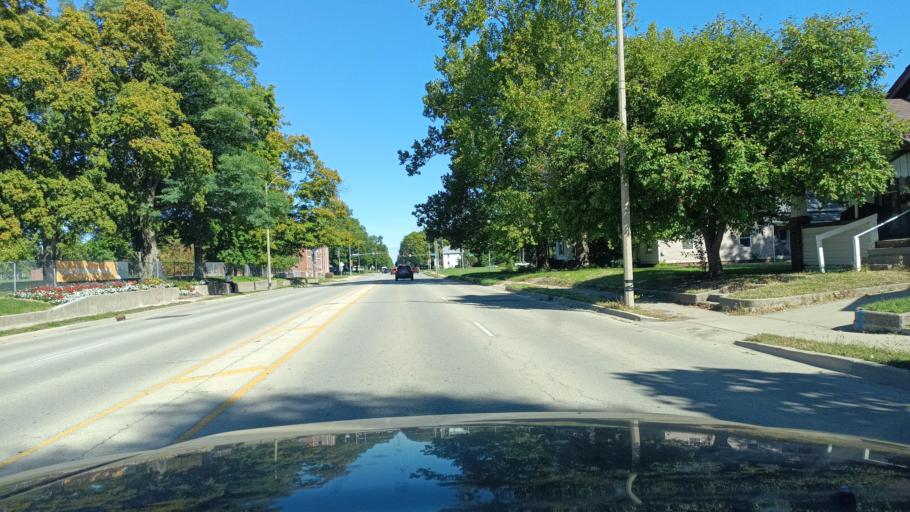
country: US
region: Illinois
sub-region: Champaign County
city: Champaign
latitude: 40.1251
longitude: -88.2435
